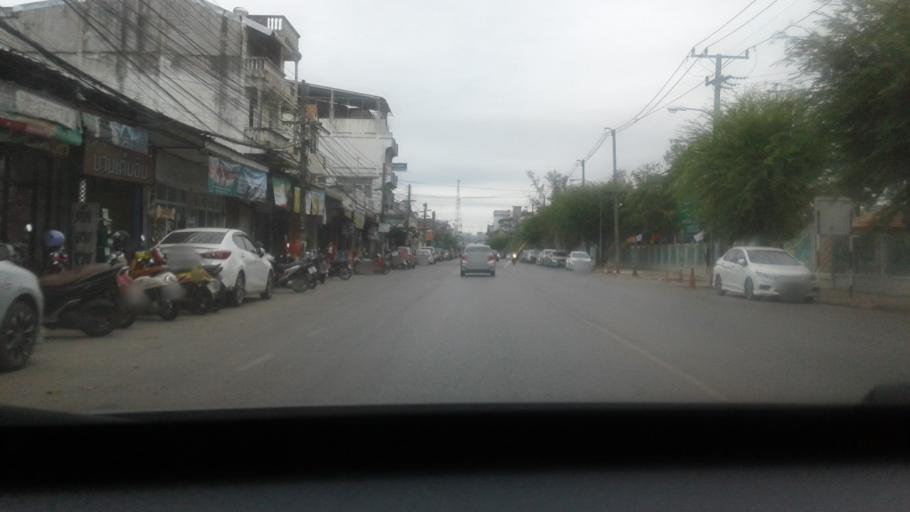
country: TH
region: Changwat Udon Thani
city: Udon Thani
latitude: 17.4010
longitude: 102.7893
